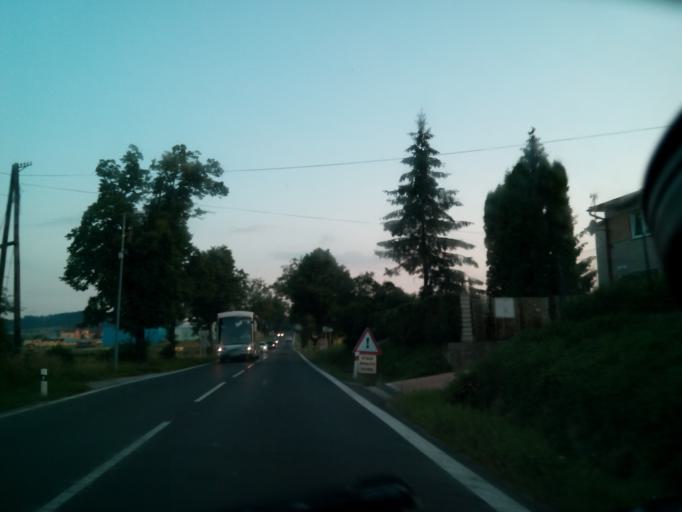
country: SK
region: Presovsky
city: Spisska Bela
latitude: 49.1693
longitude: 20.4492
